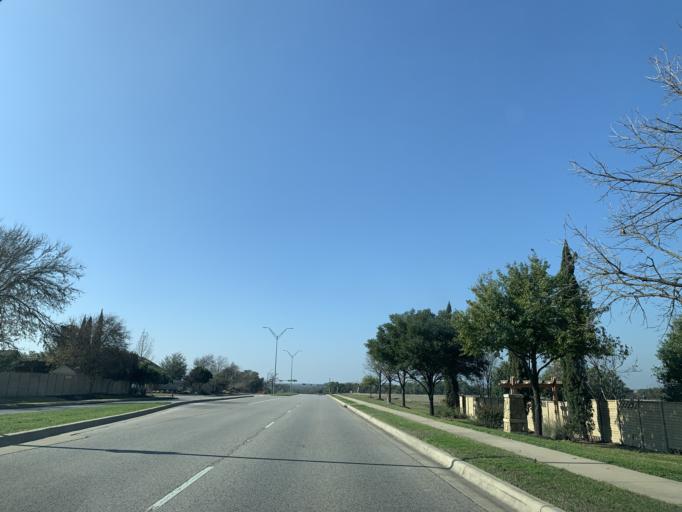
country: US
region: Texas
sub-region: Williamson County
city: Round Rock
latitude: 30.5088
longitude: -97.6336
